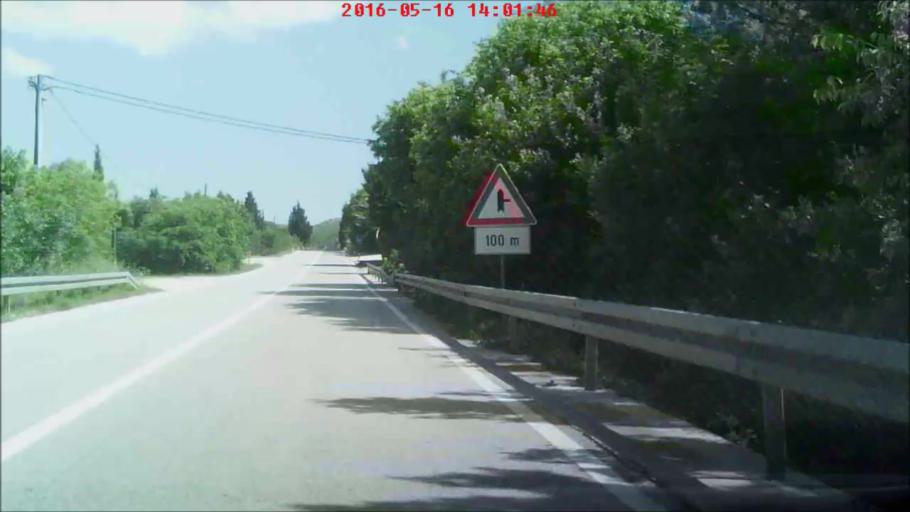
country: HR
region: Dubrovacko-Neretvanska
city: Ston
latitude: 42.8307
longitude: 17.7519
